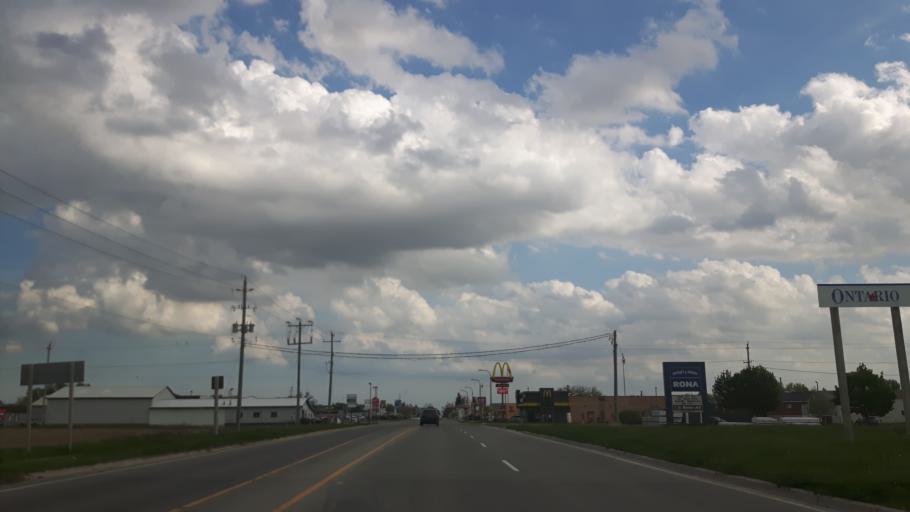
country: CA
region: Ontario
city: South Huron
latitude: 43.3647
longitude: -81.4842
